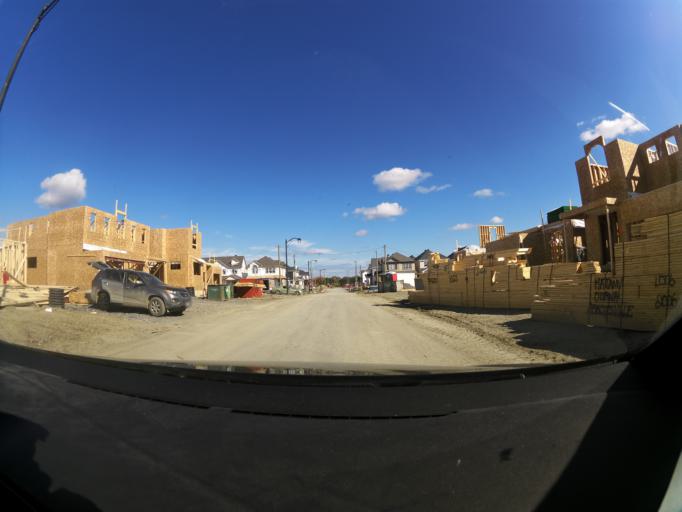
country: CA
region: Ontario
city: Bells Corners
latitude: 45.2837
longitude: -75.8925
